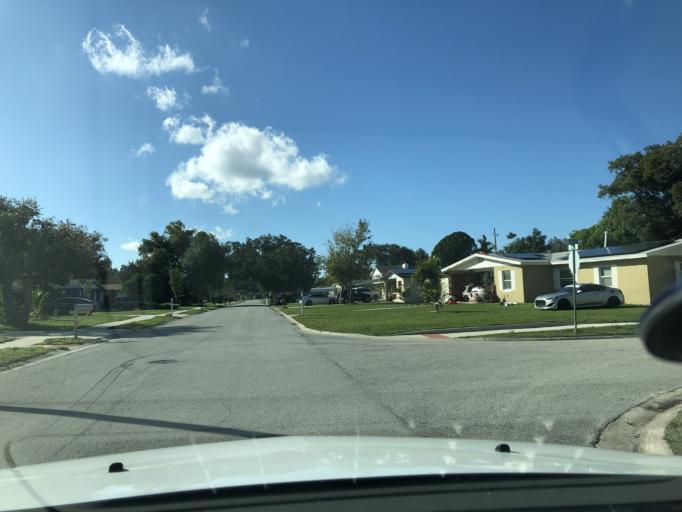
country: US
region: Florida
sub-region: Orange County
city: Oak Ridge
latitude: 28.4745
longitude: -81.4341
